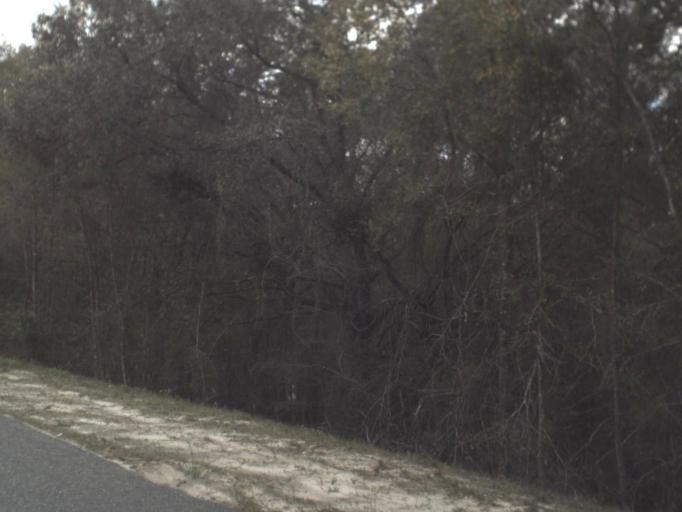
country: US
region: Florida
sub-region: Wakulla County
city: Crawfordville
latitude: 30.1626
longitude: -84.3808
